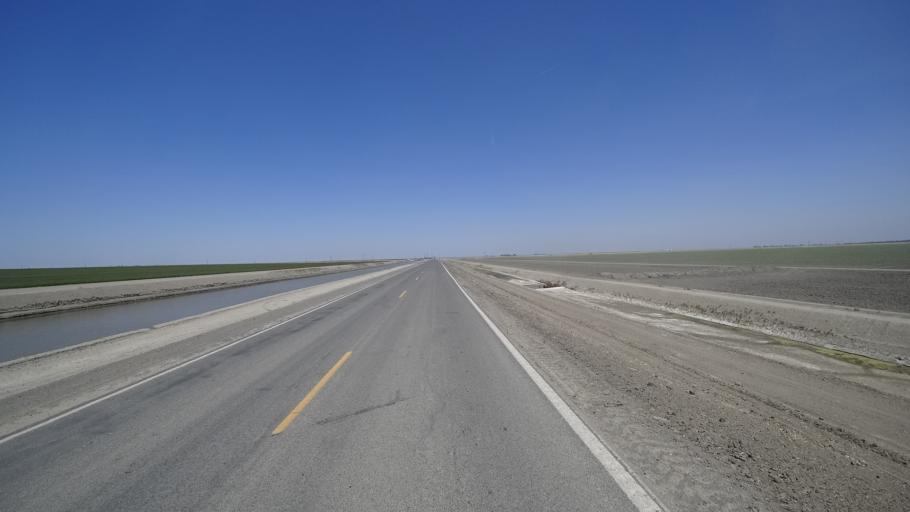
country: US
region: California
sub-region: Kings County
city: Corcoran
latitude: 36.0740
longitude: -119.6439
